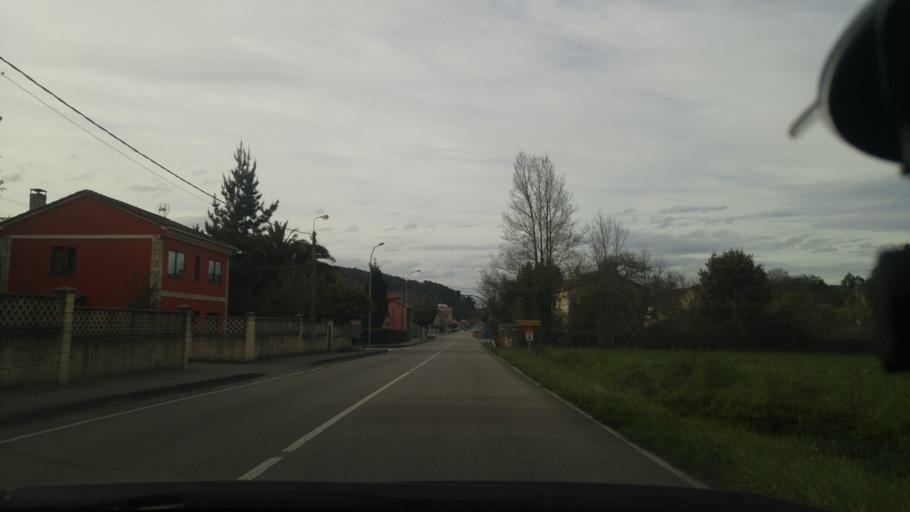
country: ES
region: Asturias
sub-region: Province of Asturias
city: Corvera de Asturias
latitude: 43.5059
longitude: -5.8664
